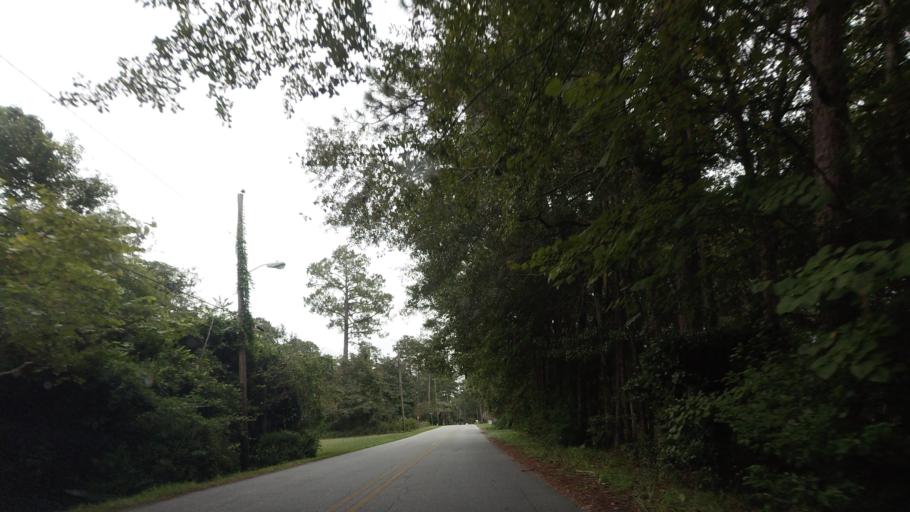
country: US
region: Georgia
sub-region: Lowndes County
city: Remerton
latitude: 30.8563
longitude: -83.2980
